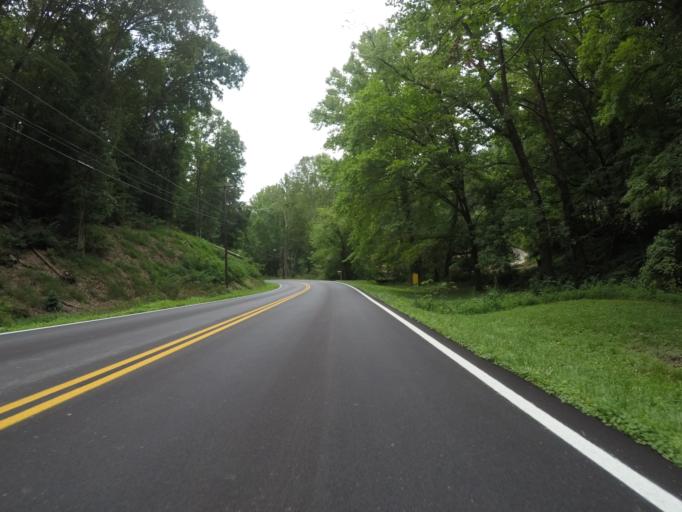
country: US
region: Kentucky
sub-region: Boyd County
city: Ashland
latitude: 38.4387
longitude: -82.6349
